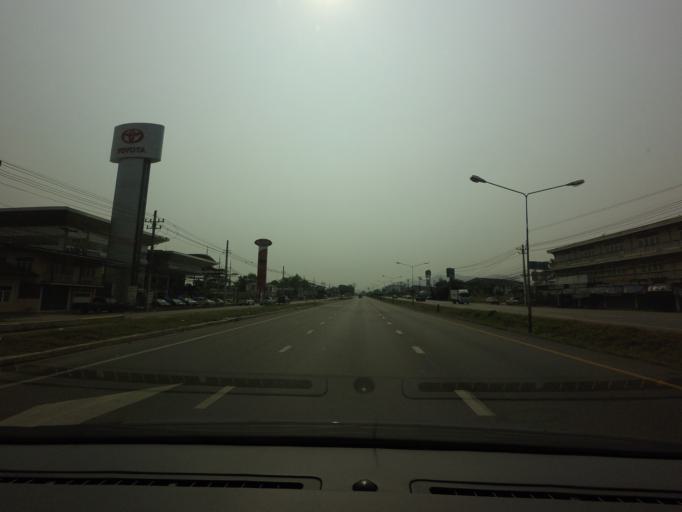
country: TH
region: Prachuap Khiri Khan
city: Pran Buri
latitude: 12.3793
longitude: 99.8917
